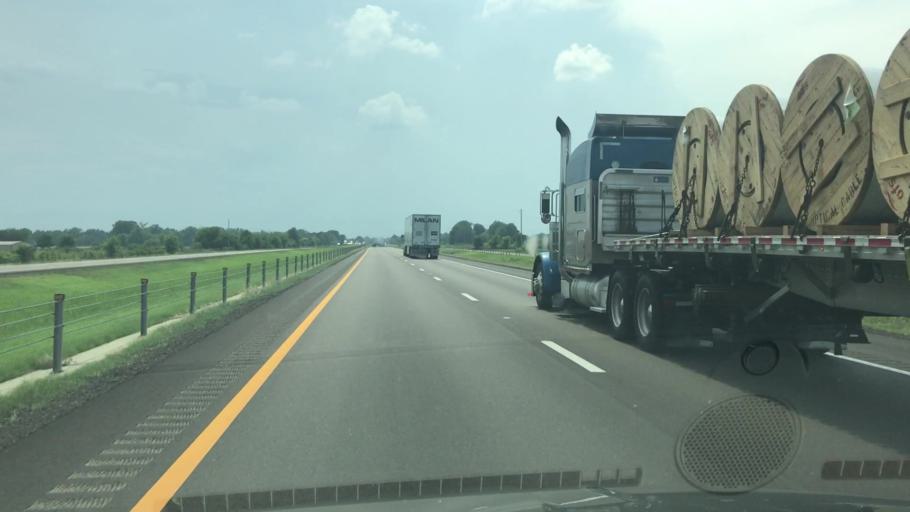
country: US
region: Arkansas
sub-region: Crittenden County
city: Earle
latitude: 35.1428
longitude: -90.4200
